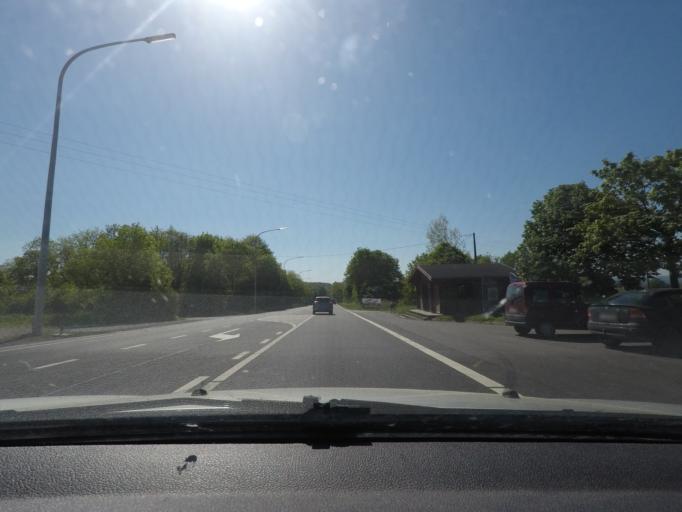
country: BE
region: Wallonia
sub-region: Province de Namur
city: Houyet
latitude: 50.1668
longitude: 5.0739
